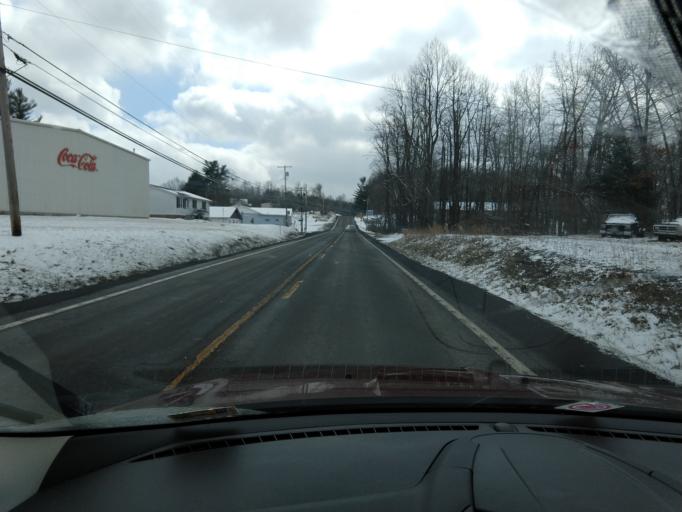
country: US
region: West Virginia
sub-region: Nicholas County
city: Craigsville
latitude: 38.3162
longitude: -80.6545
